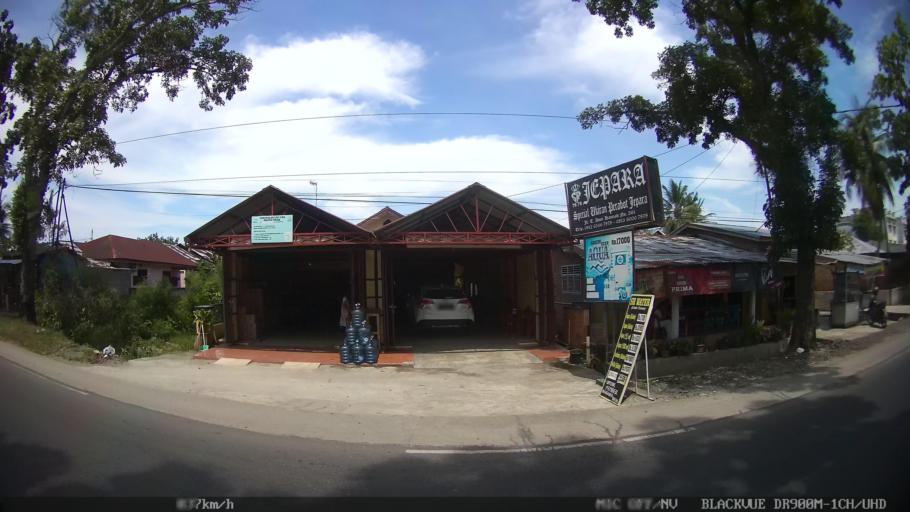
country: ID
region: North Sumatra
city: Binjai
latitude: 3.6342
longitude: 98.5105
